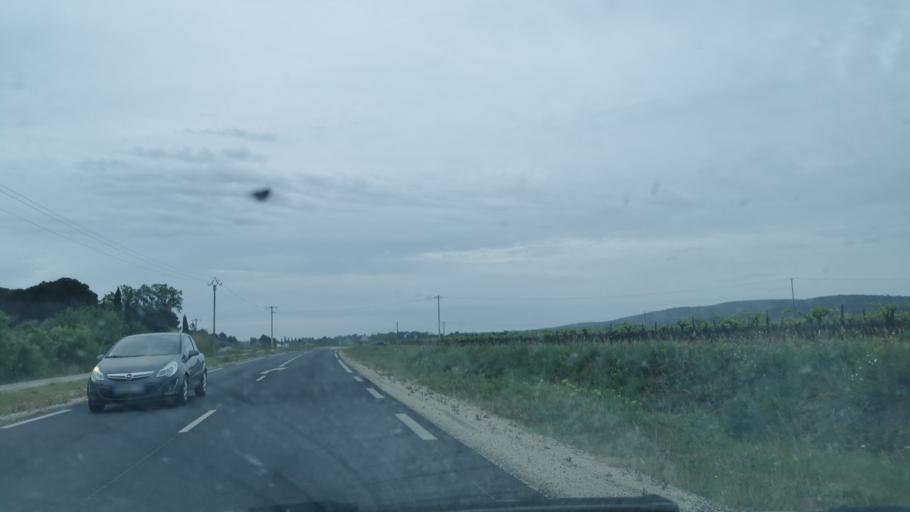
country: FR
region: Languedoc-Roussillon
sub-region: Departement de l'Herault
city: Montbazin
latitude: 43.5173
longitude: 3.6847
